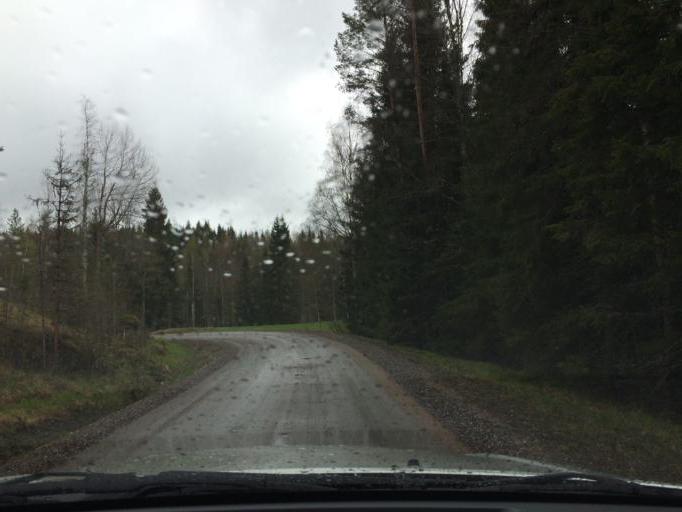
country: SE
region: Dalarna
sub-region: Ludvika Kommun
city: Abborrberget
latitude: 60.0176
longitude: 14.6147
